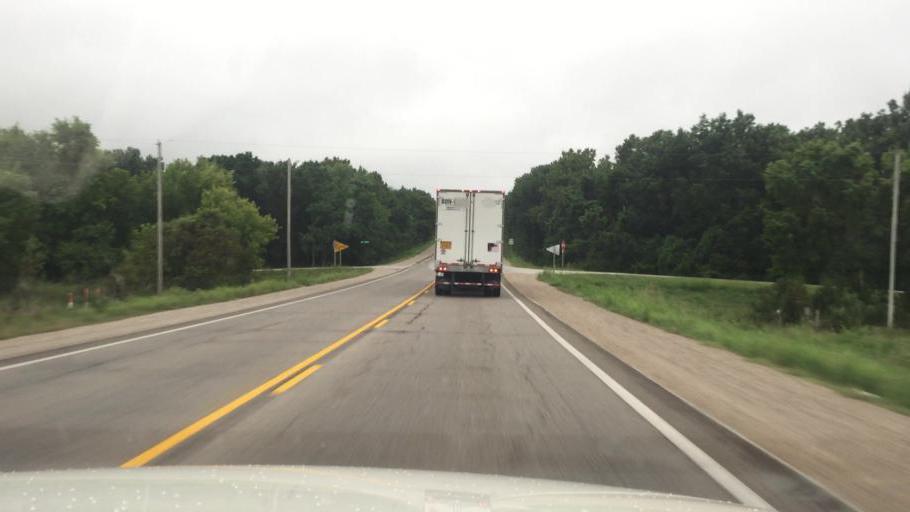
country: US
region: Kansas
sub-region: Montgomery County
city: Cherryvale
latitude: 37.1552
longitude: -95.5768
